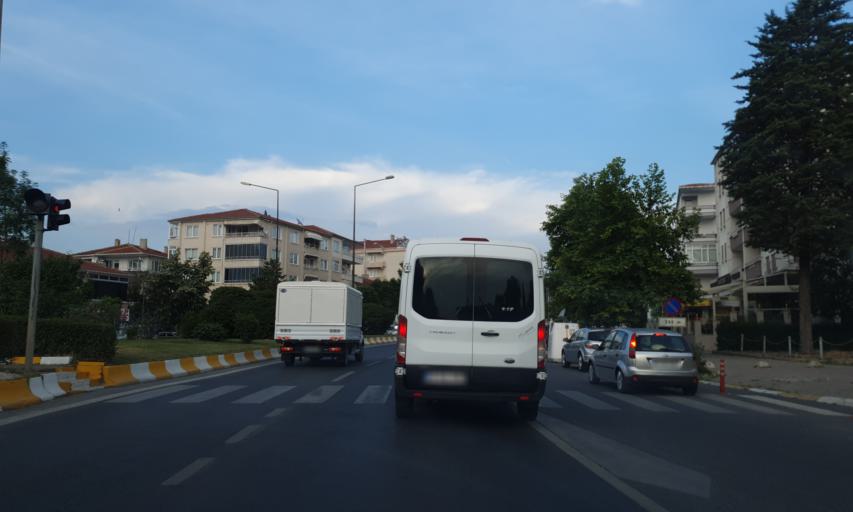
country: TR
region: Kirklareli
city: Luleburgaz
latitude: 41.4024
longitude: 27.3661
